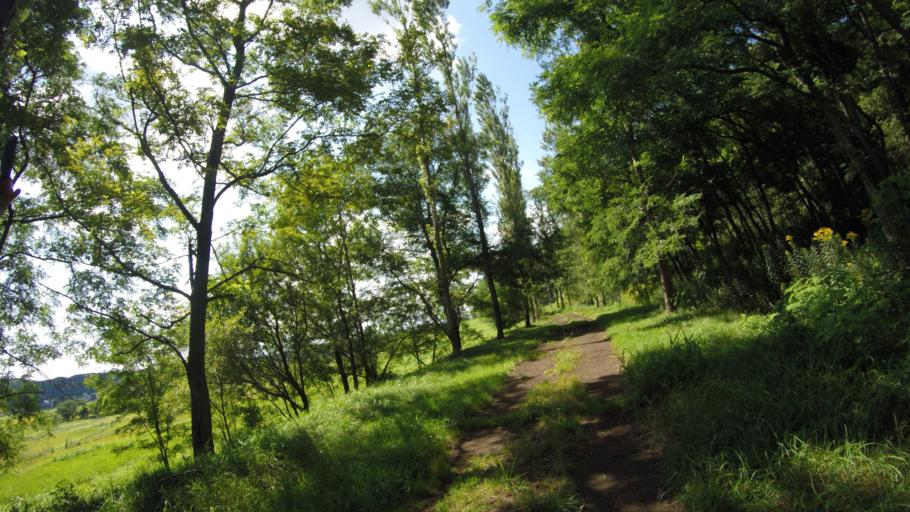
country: JP
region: Hokkaido
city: Iwamizawa
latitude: 43.1600
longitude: 141.8006
